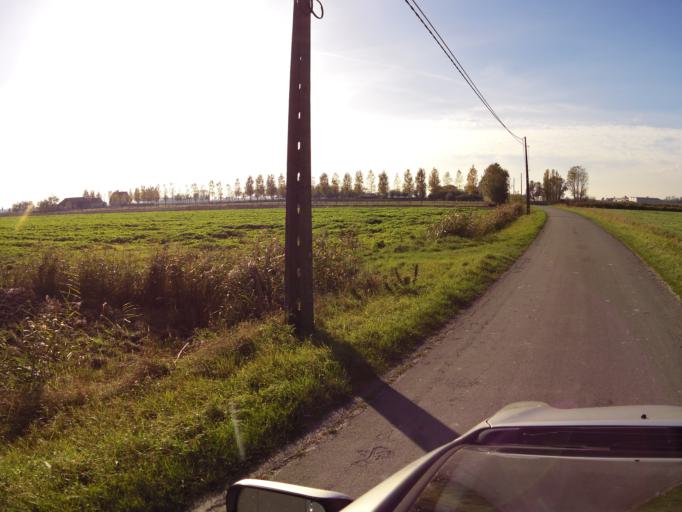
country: BE
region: Flanders
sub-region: Provincie West-Vlaanderen
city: Nieuwpoort
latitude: 51.0958
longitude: 2.7987
